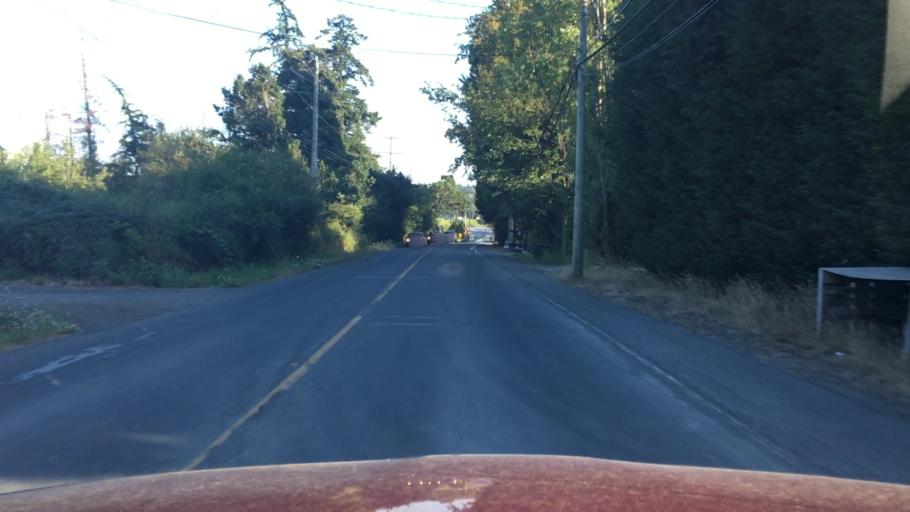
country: CA
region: British Columbia
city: Victoria
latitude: 48.4799
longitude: -123.3545
